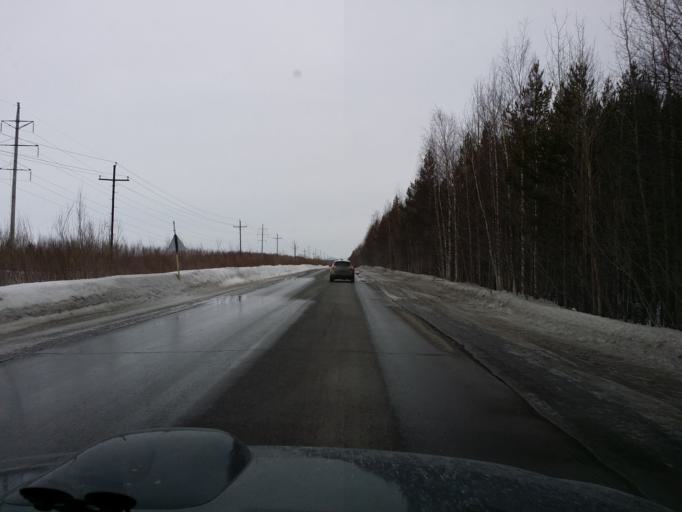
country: RU
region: Tomsk
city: Strezhevoy
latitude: 60.8023
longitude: 77.2915
